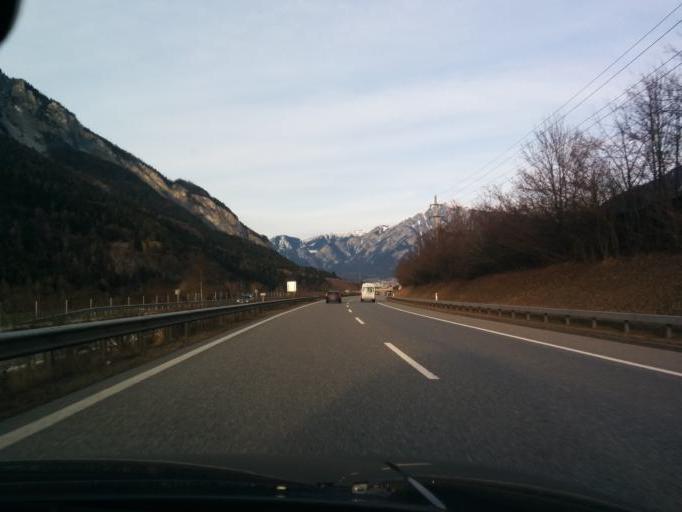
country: CH
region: Grisons
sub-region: Imboden District
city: Domat
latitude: 46.8351
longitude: 9.4386
